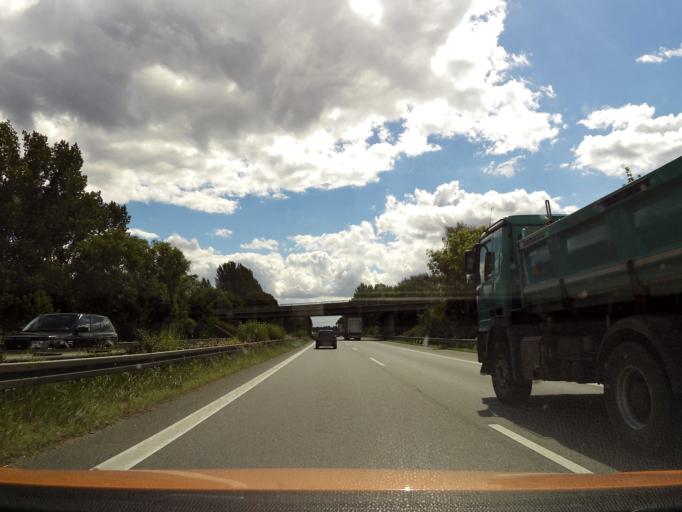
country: DE
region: Berlin
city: Blankenfelde
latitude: 52.6629
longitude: 13.4087
